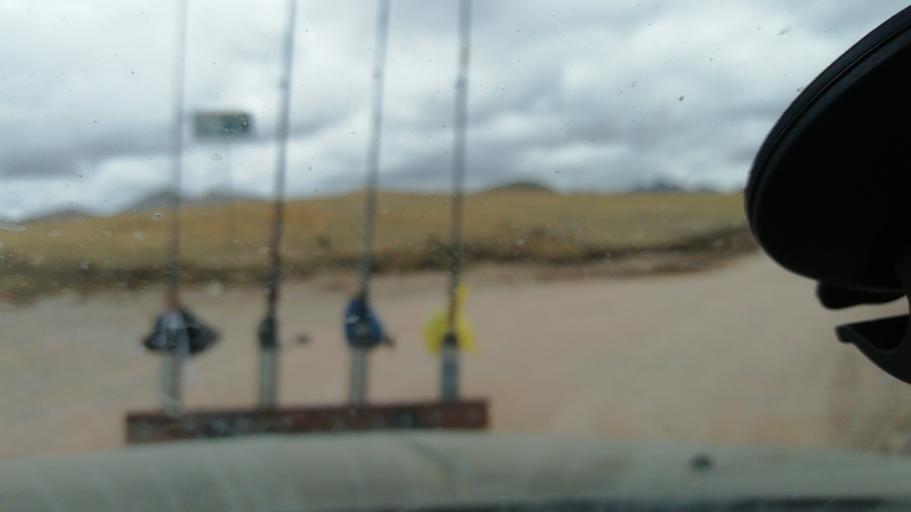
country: PE
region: Huancavelica
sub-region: Provincia de Huancavelica
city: Acobambilla
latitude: -12.5430
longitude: -75.5468
